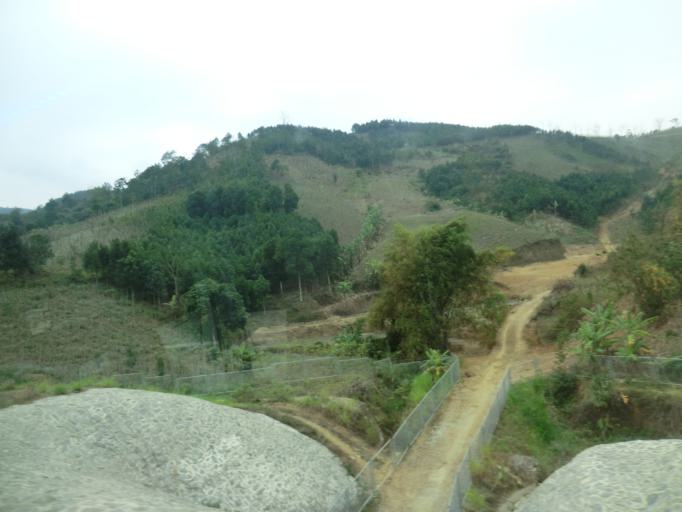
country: VN
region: Lao Cai
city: Thi Tran Pho Rang
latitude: 22.0316
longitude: 104.5000
